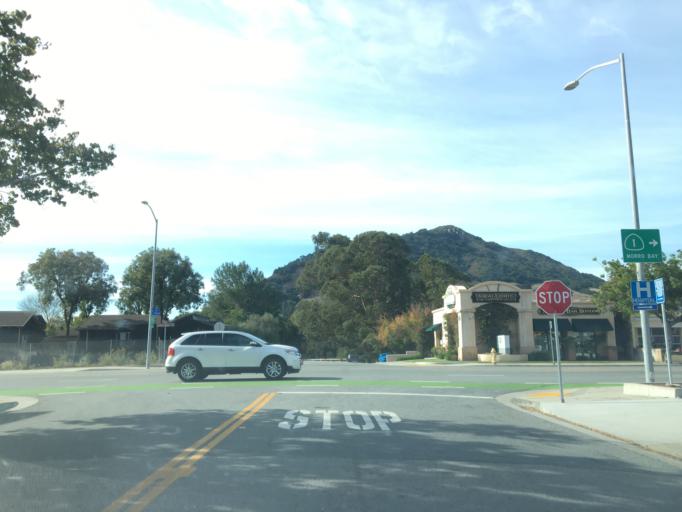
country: US
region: California
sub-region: San Luis Obispo County
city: San Luis Obispo
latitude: 35.2885
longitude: -120.6647
